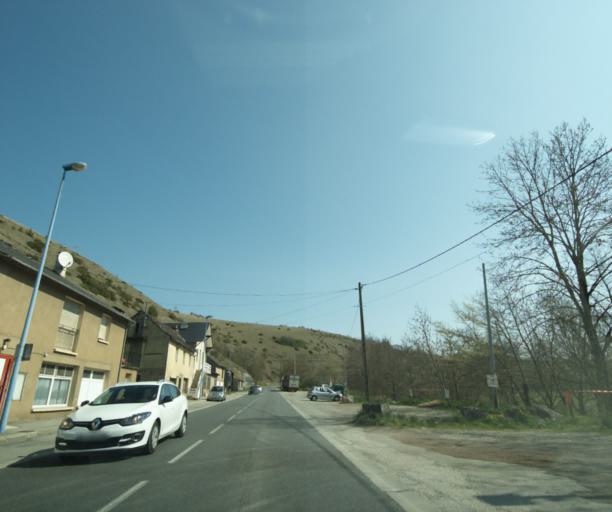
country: FR
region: Midi-Pyrenees
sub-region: Departement de l'Aveyron
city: Sainte-Radegonde
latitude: 44.3717
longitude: 2.6332
